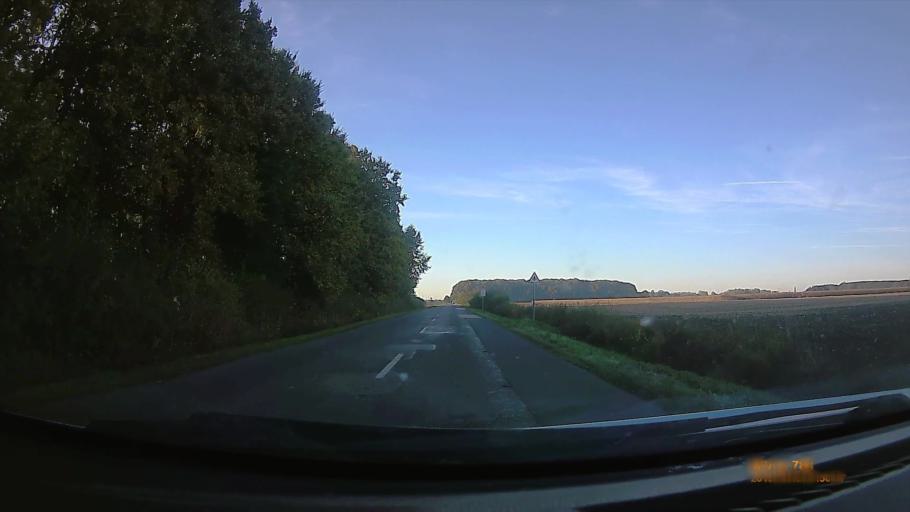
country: HU
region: Hajdu-Bihar
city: Biharkeresztes
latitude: 47.1522
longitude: 21.7376
